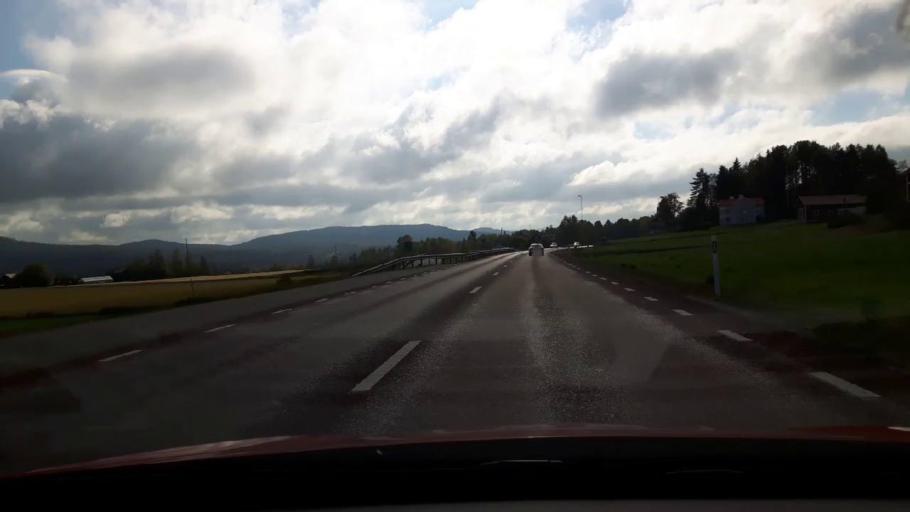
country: SE
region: Gaevleborg
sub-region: Ljusdals Kommun
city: Jaervsoe
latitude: 61.7287
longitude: 16.1669
